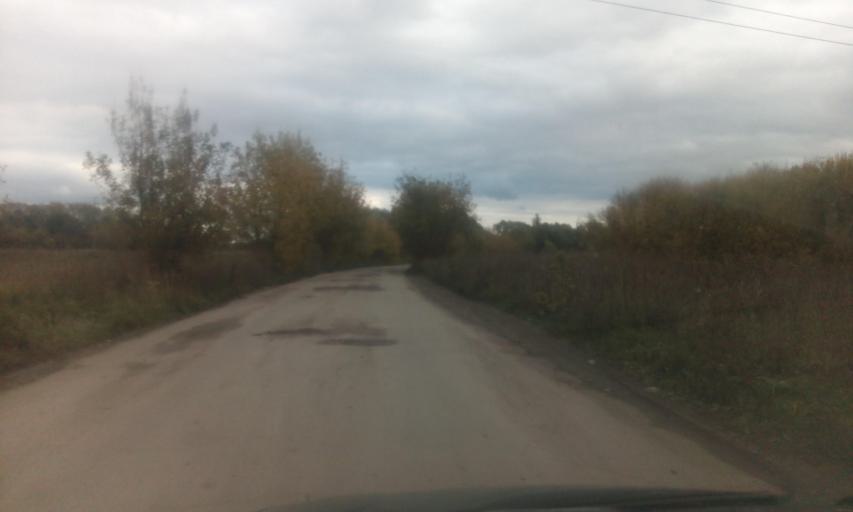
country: RU
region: Tula
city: Gritsovskiy
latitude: 54.1279
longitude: 38.1638
